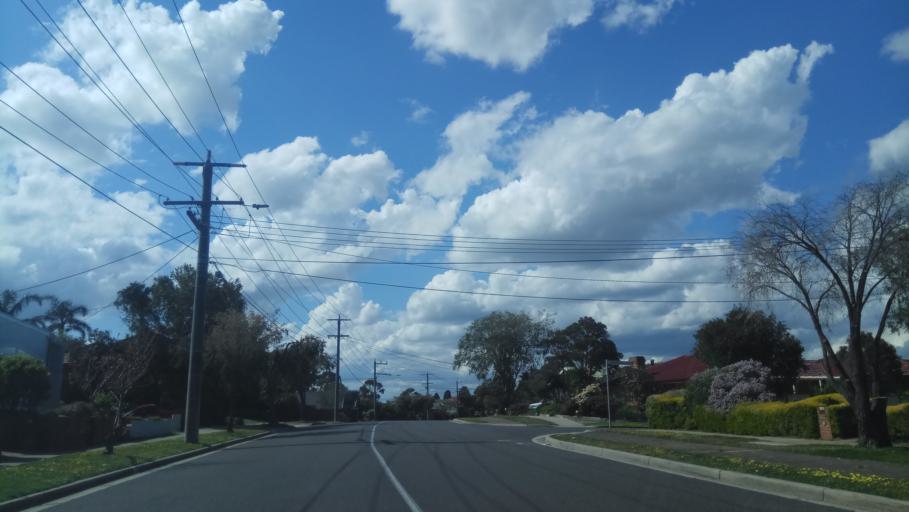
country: AU
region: Victoria
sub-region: Kingston
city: Dingley Village
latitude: -37.9762
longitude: 145.1172
